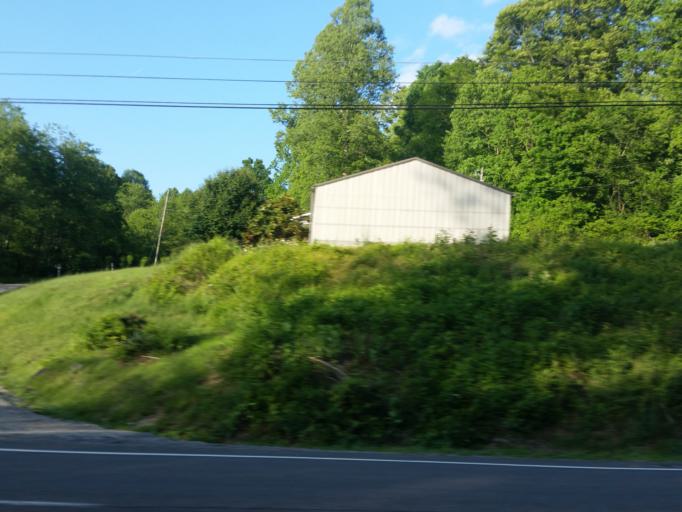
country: US
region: Virginia
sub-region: Washington County
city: Abingdon
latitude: 36.7405
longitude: -82.0410
